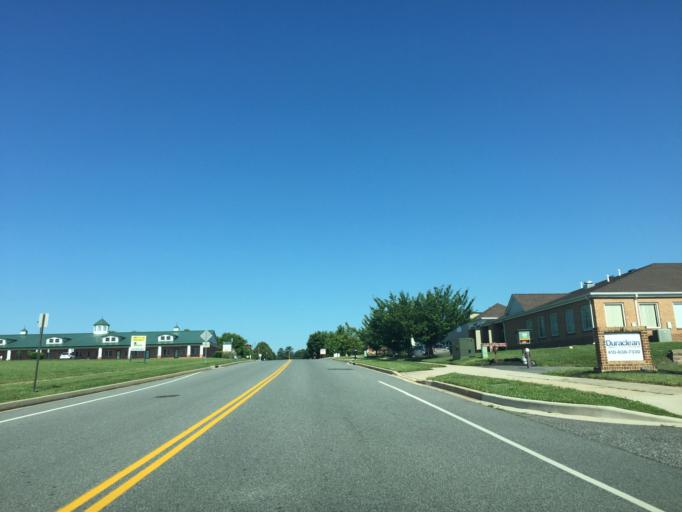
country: US
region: Maryland
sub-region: Harford County
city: Bel Air North
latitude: 39.5778
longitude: -76.3808
